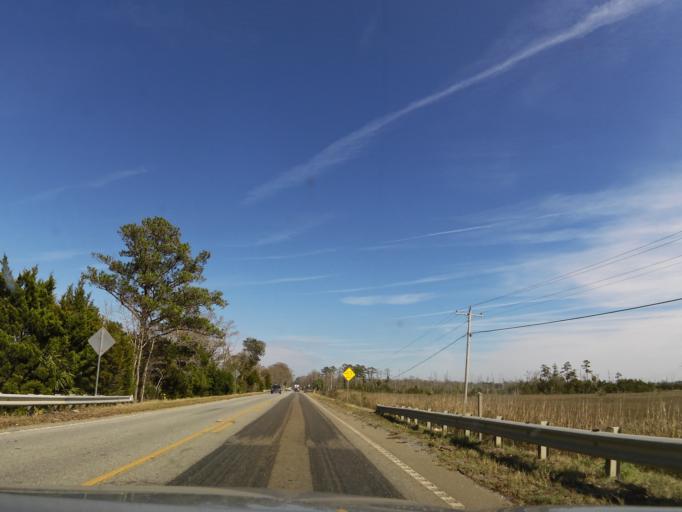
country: US
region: Georgia
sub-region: Glynn County
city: Dock Junction
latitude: 31.2650
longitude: -81.5932
